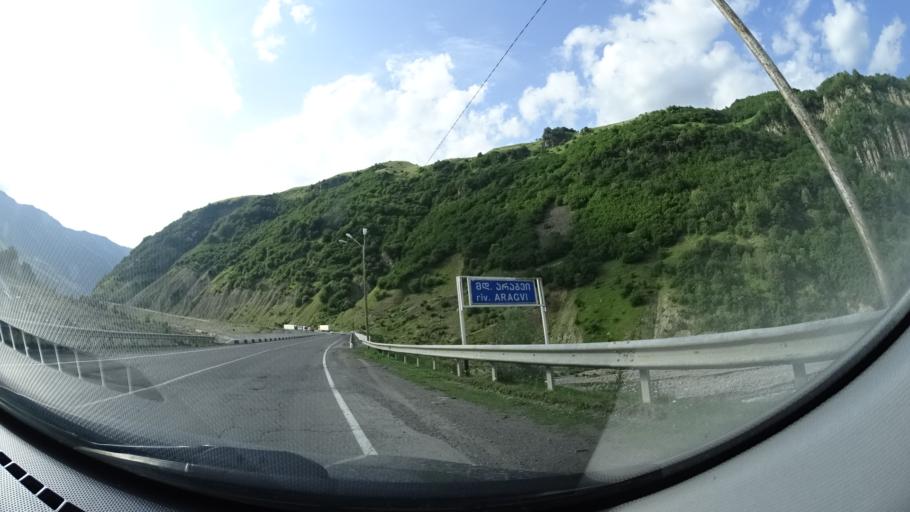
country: GE
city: Gudauri
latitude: 42.4296
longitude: 44.5097
